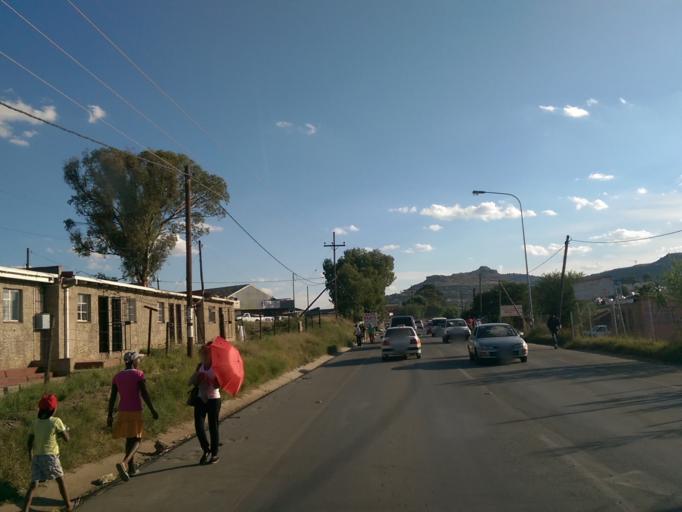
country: LS
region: Maseru
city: Maseru
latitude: -29.3094
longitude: 27.5132
